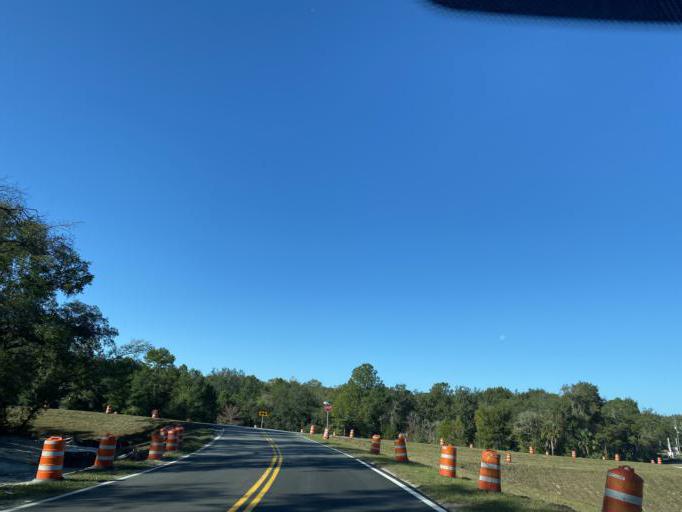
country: US
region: Florida
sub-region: Lake County
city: Mount Plymouth
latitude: 28.8297
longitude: -81.5205
